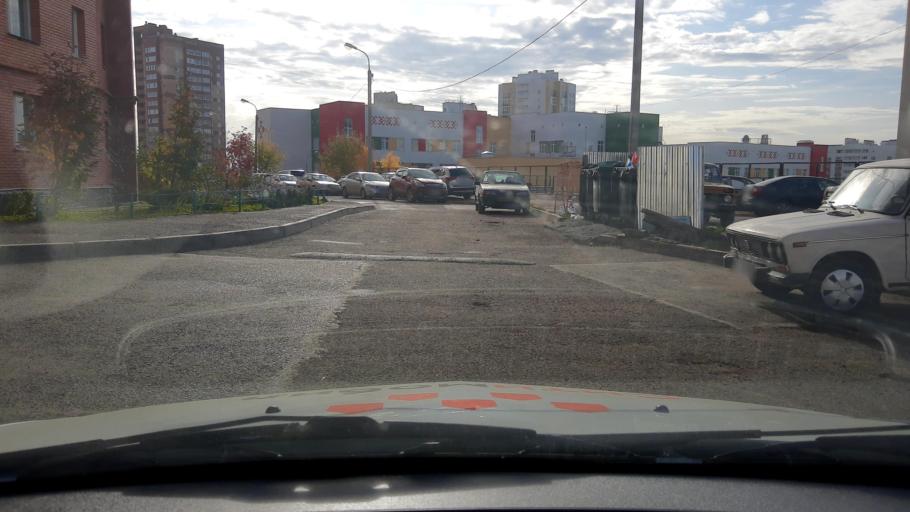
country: RU
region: Bashkortostan
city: Ufa
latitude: 54.6914
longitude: 55.9945
